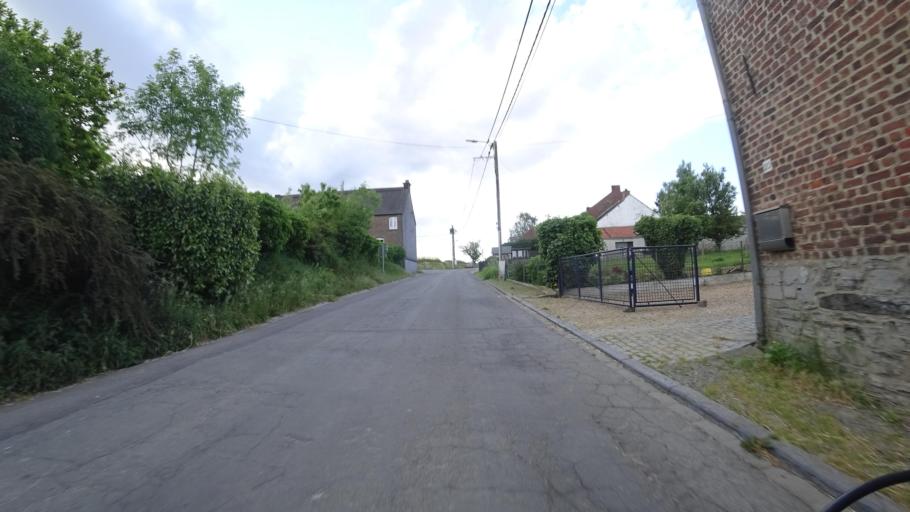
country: BE
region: Wallonia
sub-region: Province de Namur
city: Gembloux
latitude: 50.5503
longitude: 4.7300
